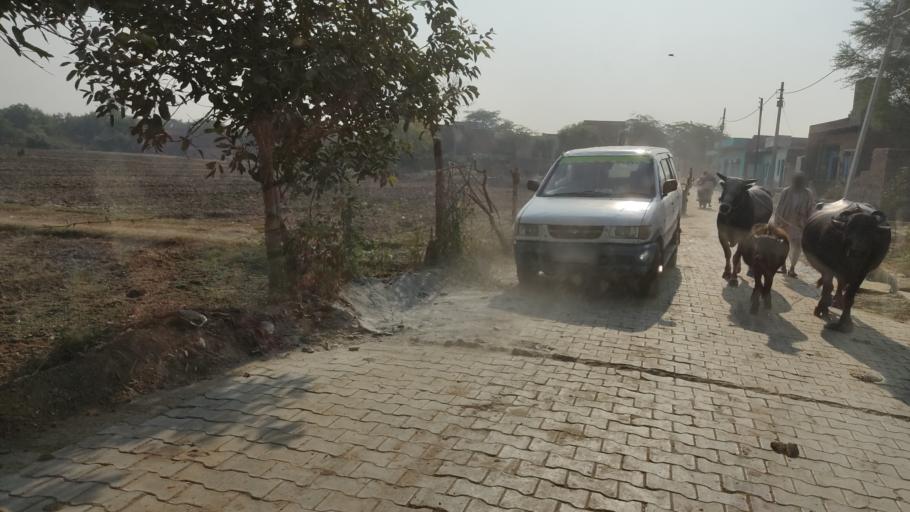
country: IN
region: Uttar Pradesh
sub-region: Mathura
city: Radha Kund
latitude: 27.5608
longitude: 77.5582
